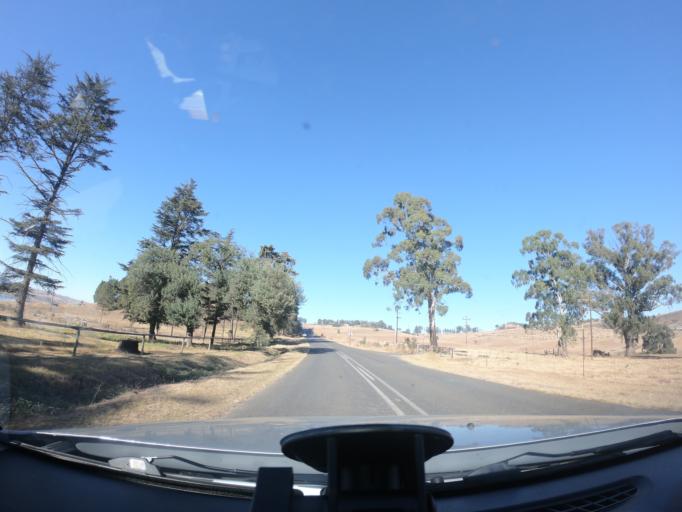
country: ZA
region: KwaZulu-Natal
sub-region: uMgungundlovu District Municipality
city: Mooirivier
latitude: -29.3180
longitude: 29.9212
